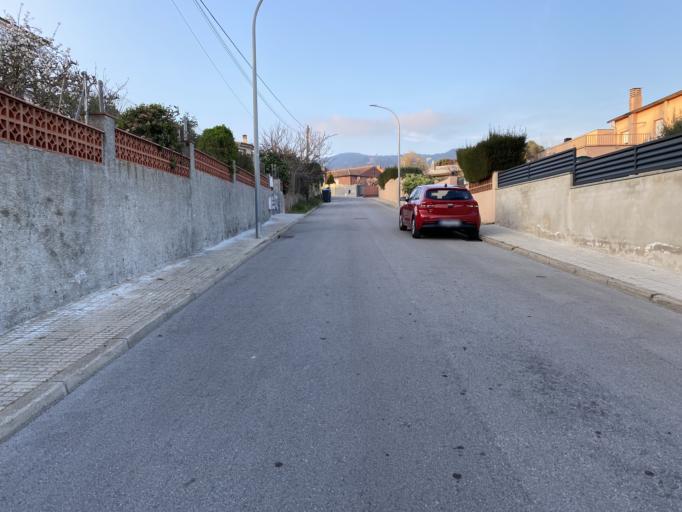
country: ES
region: Catalonia
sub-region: Provincia de Barcelona
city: Viladecavalls
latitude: 41.5594
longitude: 1.9521
